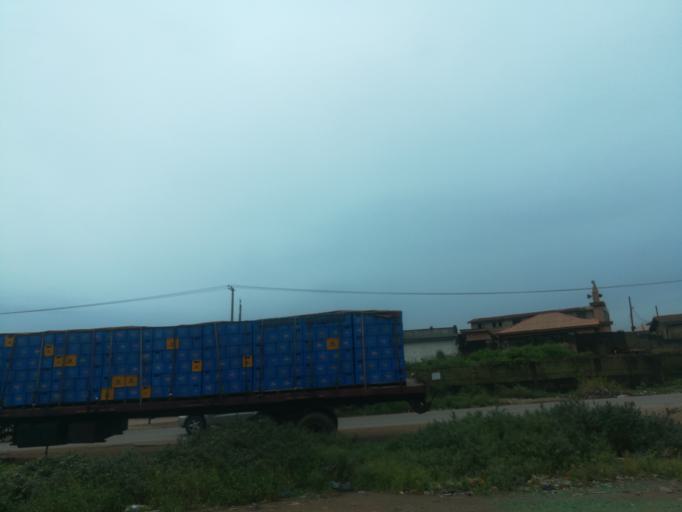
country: NG
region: Oyo
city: Ibadan
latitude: 7.3664
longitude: 3.9278
